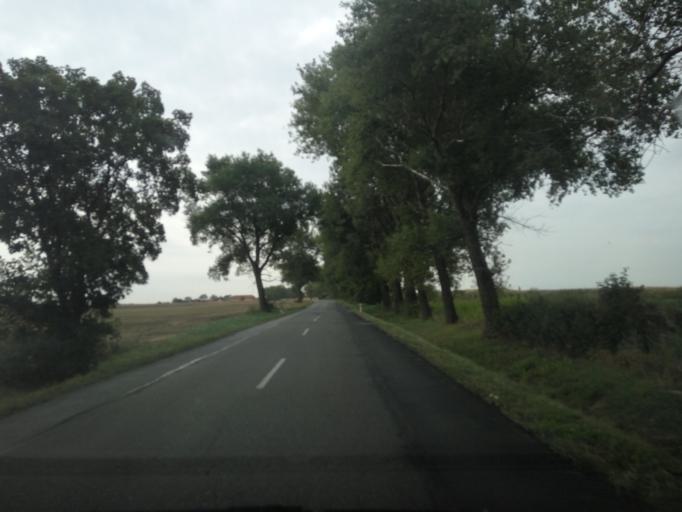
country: PL
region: Lower Silesian Voivodeship
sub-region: Powiat wroclawski
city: Zorawina
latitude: 50.9022
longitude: 17.0622
